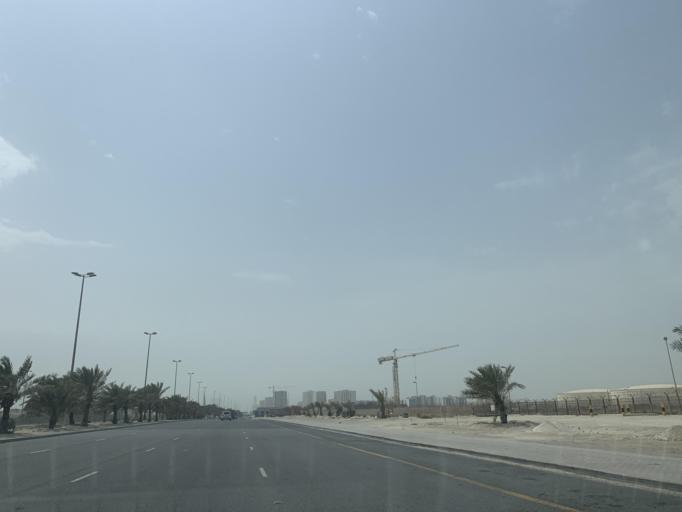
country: BH
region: Muharraq
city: Al Hadd
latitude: 26.2255
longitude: 50.6669
